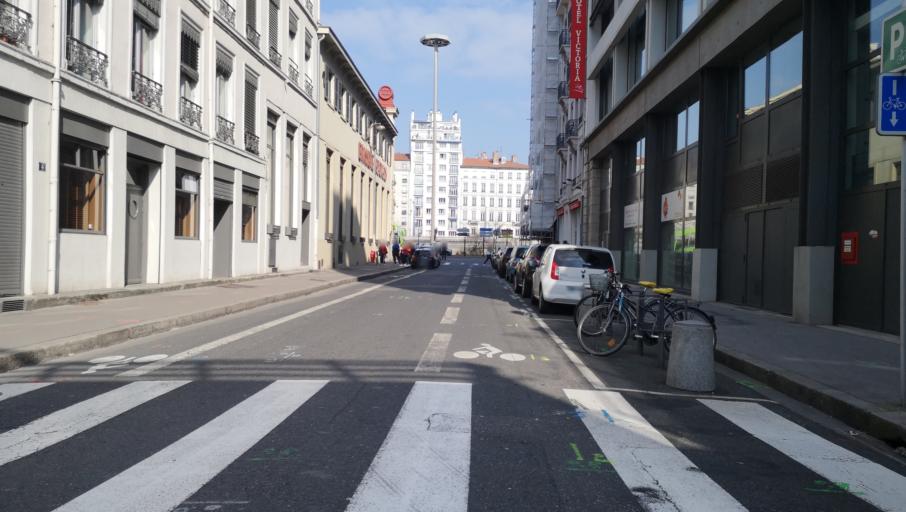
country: FR
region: Rhone-Alpes
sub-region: Departement du Rhone
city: Lyon
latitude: 45.7476
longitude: 4.8280
